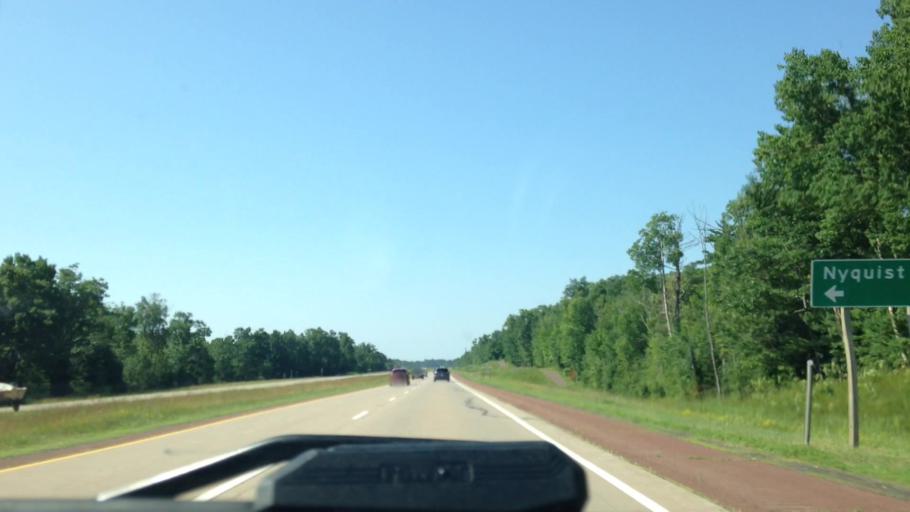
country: US
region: Wisconsin
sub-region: Douglas County
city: Lake Nebagamon
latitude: 46.3772
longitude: -91.8250
